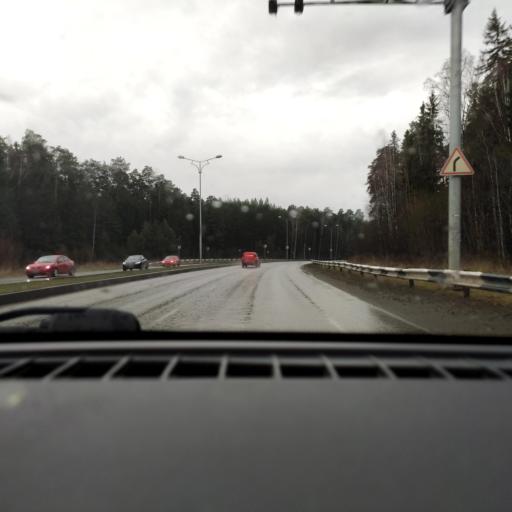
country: RU
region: Perm
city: Kondratovo
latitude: 58.0221
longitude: 55.9945
